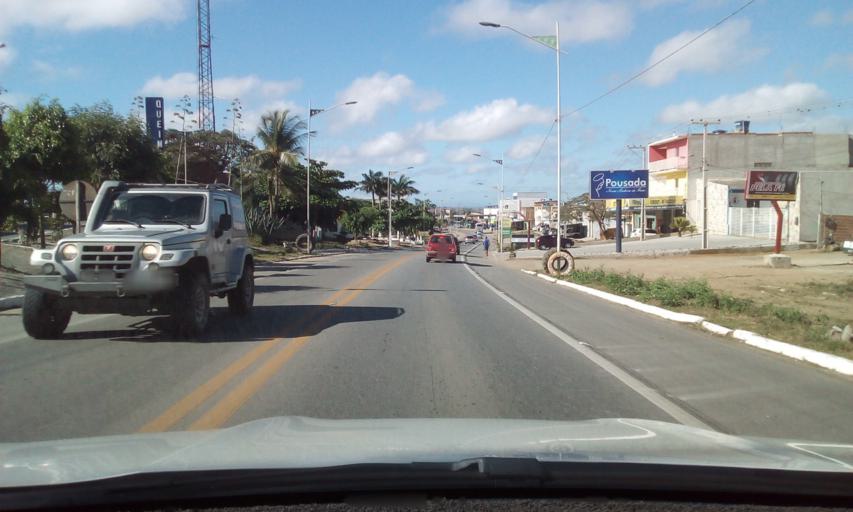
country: BR
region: Paraiba
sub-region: Fagundes
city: Fagundes
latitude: -7.3596
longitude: -35.9019
